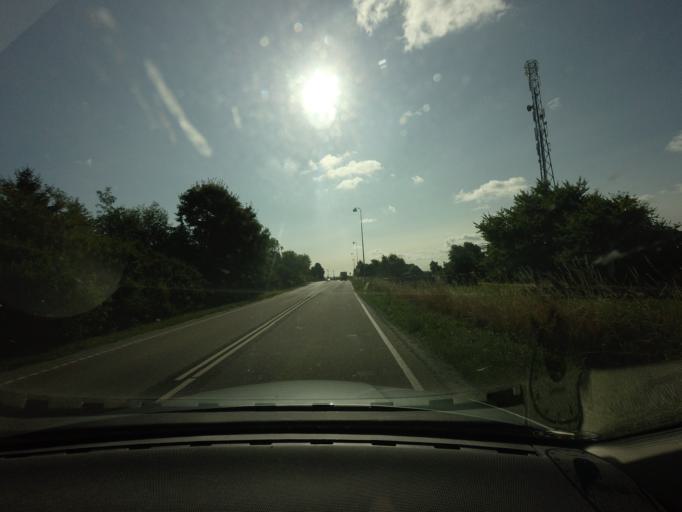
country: DK
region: Zealand
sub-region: Vordingborg Kommune
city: Praesto
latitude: 55.0067
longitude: 12.1428
